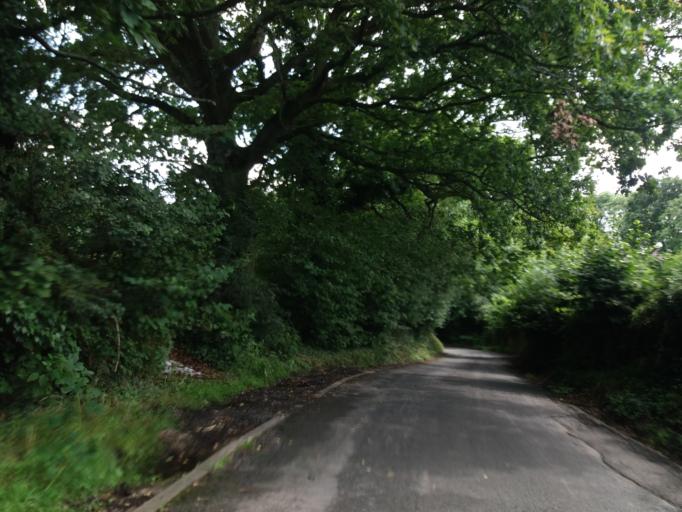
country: GB
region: England
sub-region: Lancashire
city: Euxton
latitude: 53.6648
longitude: -2.6650
